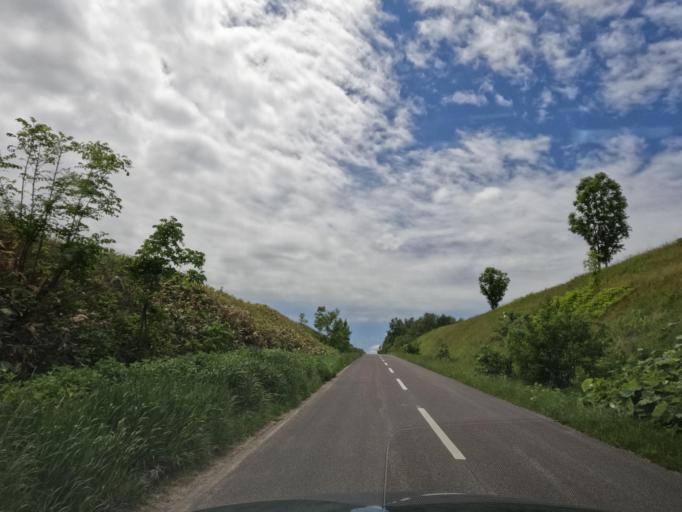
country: JP
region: Hokkaido
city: Shimo-furano
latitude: 43.5110
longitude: 142.4221
